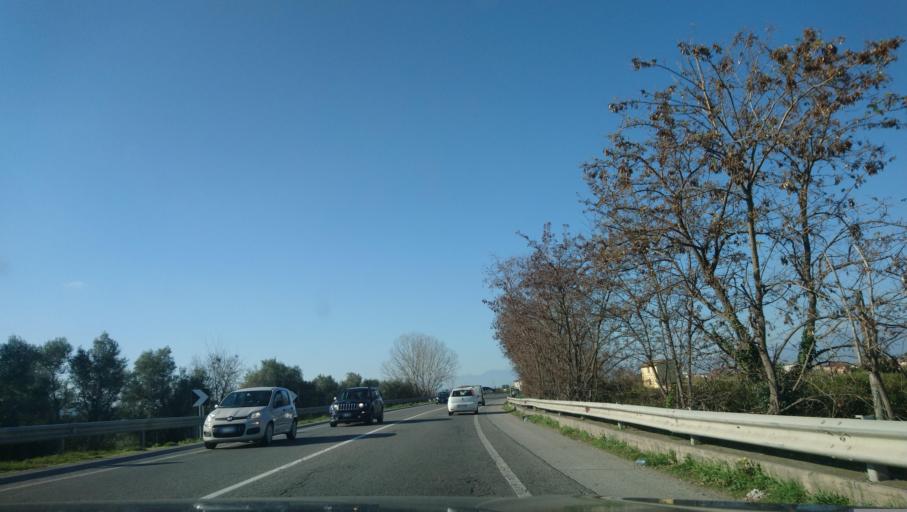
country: IT
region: Calabria
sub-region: Provincia di Cosenza
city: Fabrizio
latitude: 39.6329
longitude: 16.5550
